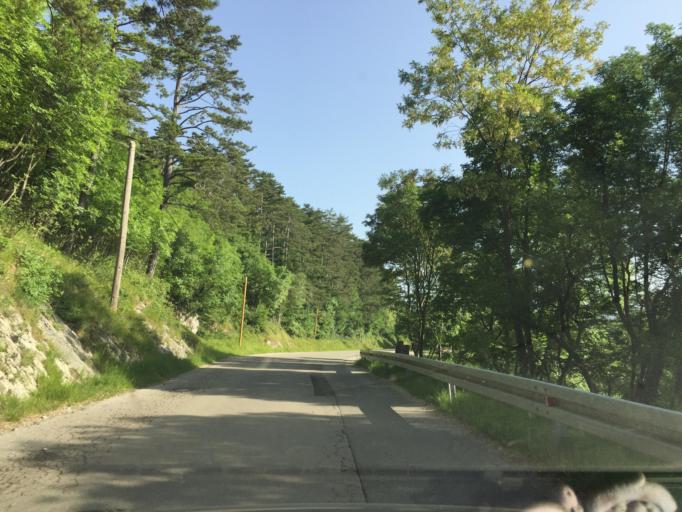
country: HR
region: Primorsko-Goranska
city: Klana
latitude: 45.4564
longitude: 14.3780
